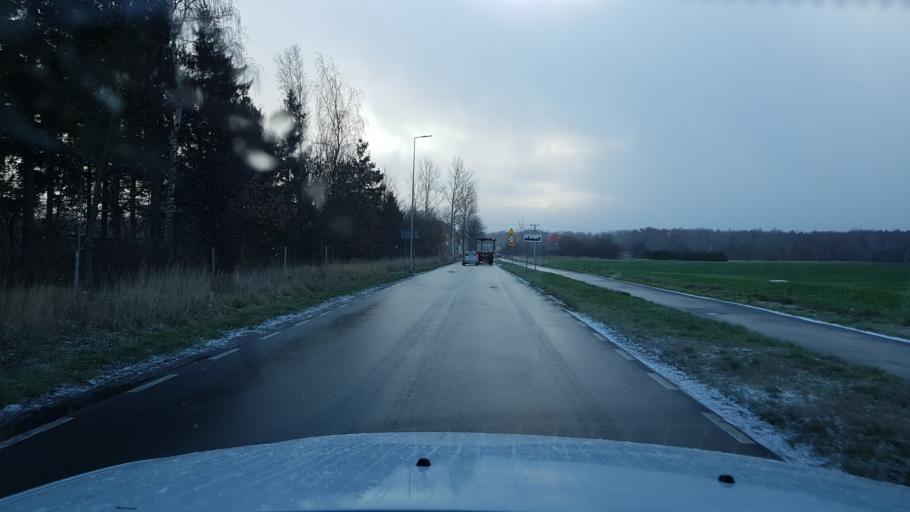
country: PL
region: West Pomeranian Voivodeship
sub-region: Powiat gryficki
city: Trzebiatow
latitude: 54.0542
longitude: 15.3025
